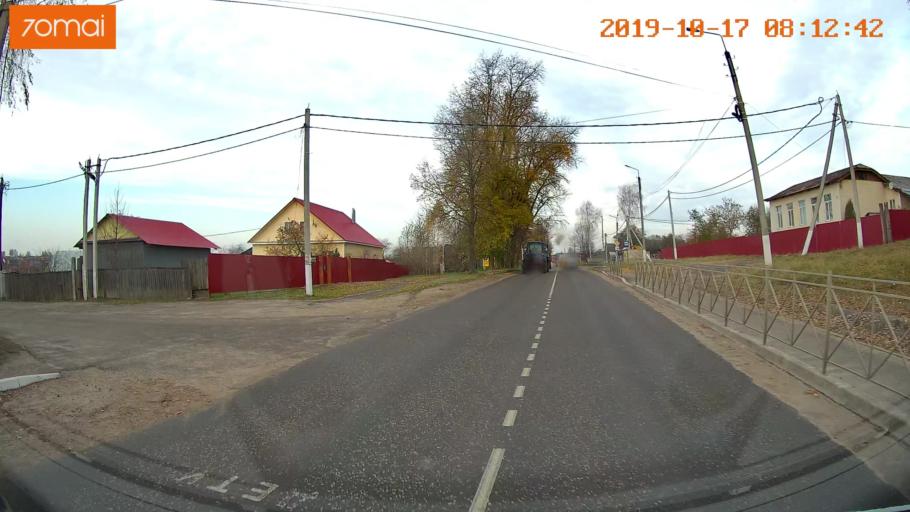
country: RU
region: Vladimir
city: Kol'chugino
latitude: 56.2995
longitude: 39.3554
